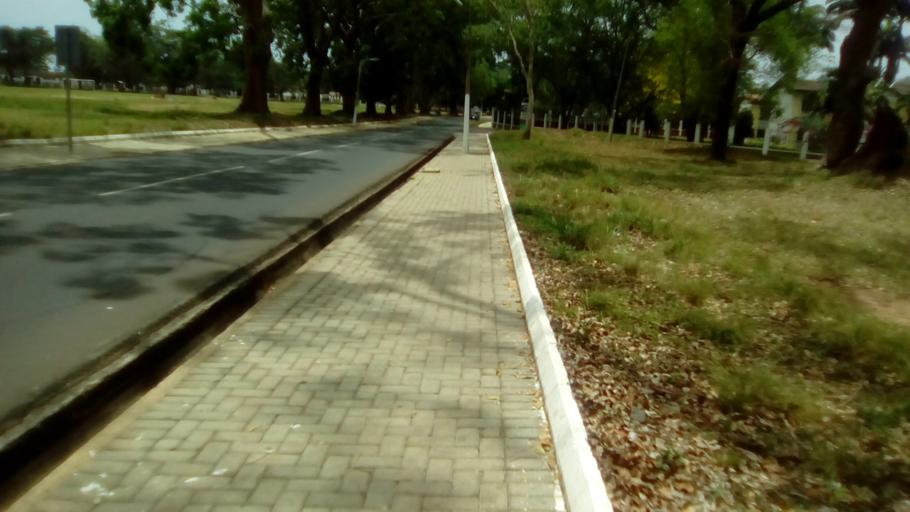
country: GH
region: Greater Accra
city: Medina Estates
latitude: 5.6457
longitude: -0.1891
